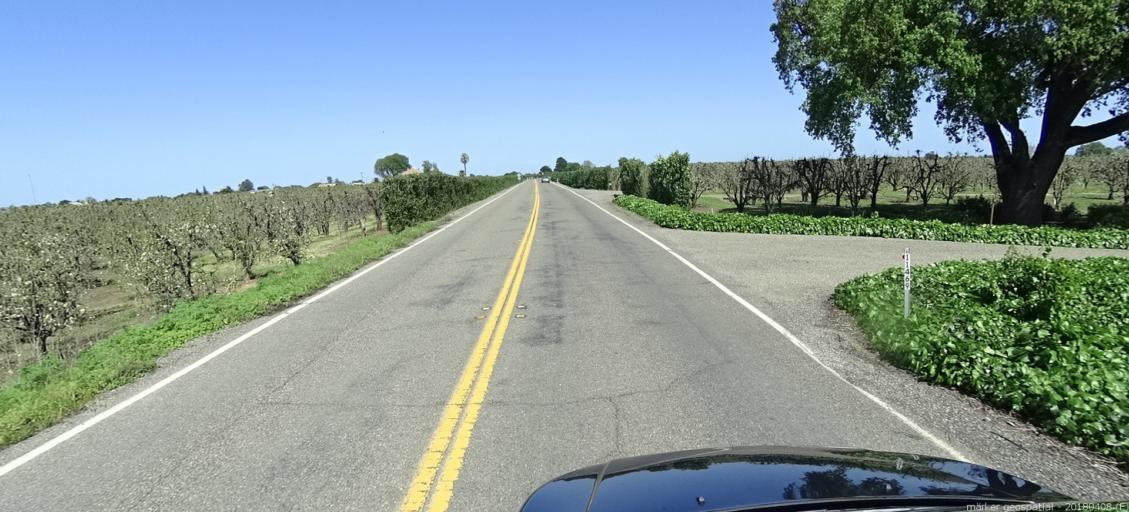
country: US
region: California
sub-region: Sacramento County
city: Walnut Grove
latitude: 38.3363
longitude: -121.5504
